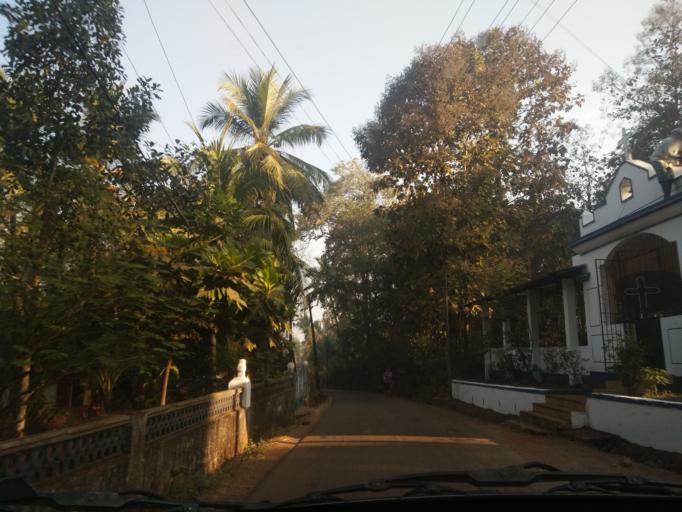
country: IN
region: Goa
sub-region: South Goa
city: Davorlim
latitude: 15.2876
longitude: 74.0073
